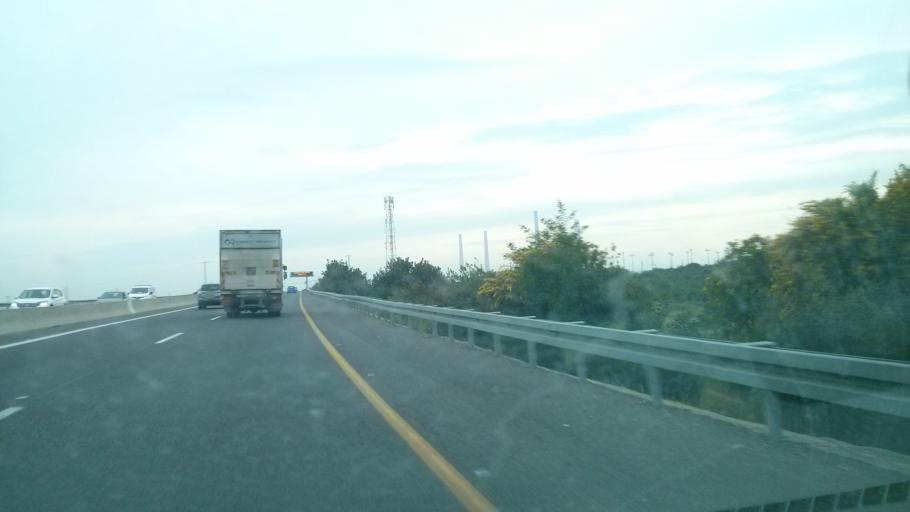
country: IL
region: Haifa
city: Qesarya
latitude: 32.4875
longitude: 34.9157
